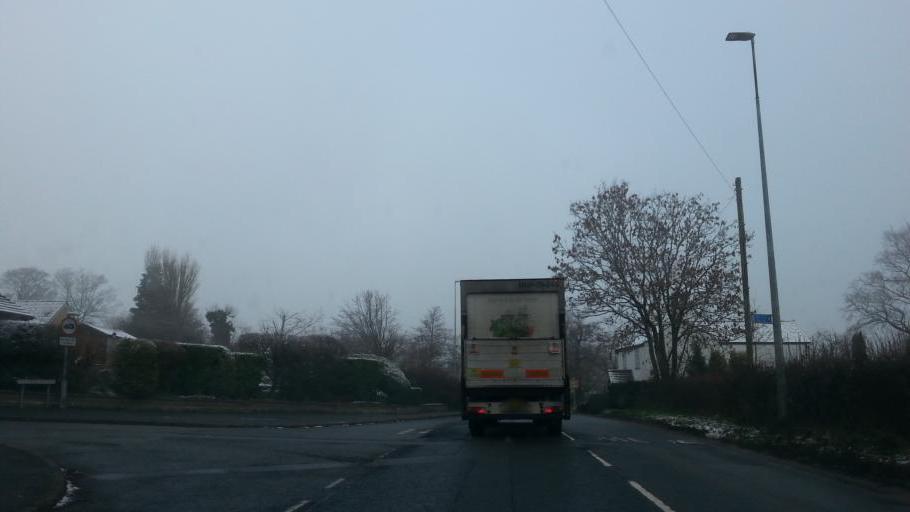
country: GB
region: England
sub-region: Cheshire East
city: Eaton
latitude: 53.1761
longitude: -2.2090
